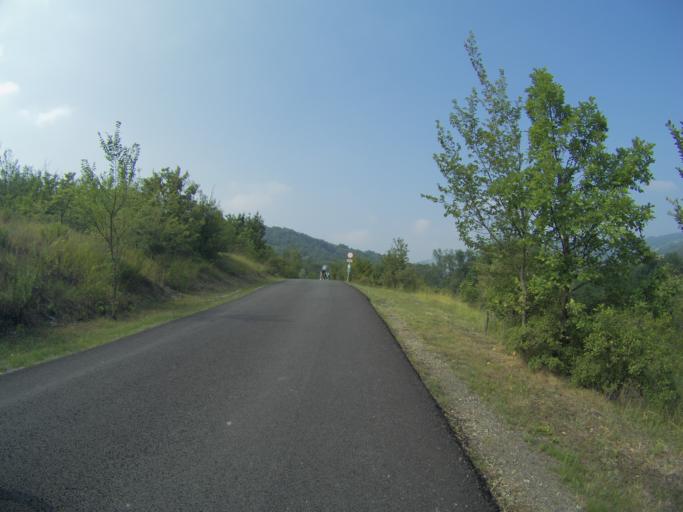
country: IT
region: Emilia-Romagna
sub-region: Provincia di Reggio Emilia
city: Ventoso
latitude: 44.5841
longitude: 10.6689
